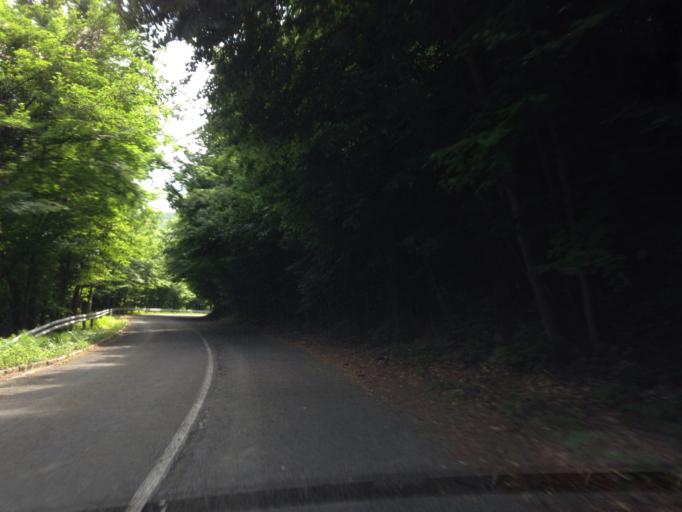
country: HU
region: Pest
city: Visegrad
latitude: 47.7331
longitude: 18.9554
